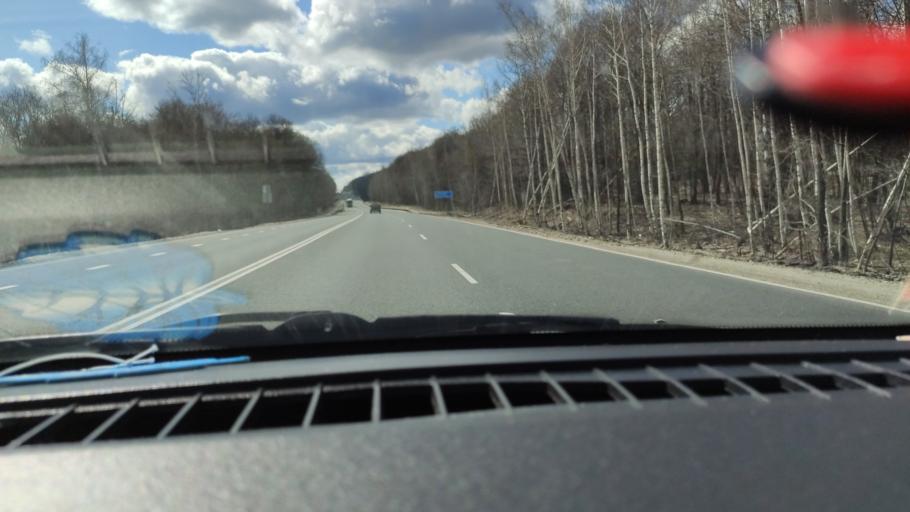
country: RU
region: Saratov
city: Khvalynsk
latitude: 52.5084
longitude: 48.0157
